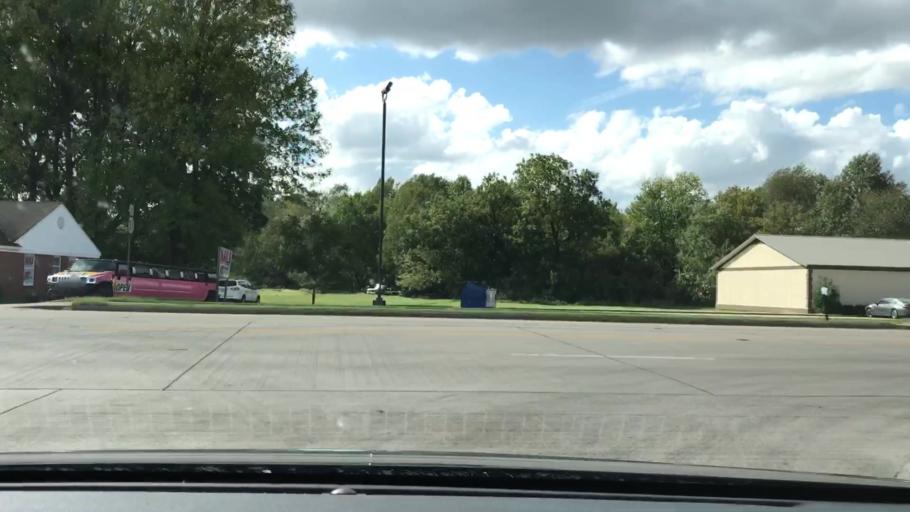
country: US
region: Kentucky
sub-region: Graves County
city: Mayfield
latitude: 36.7563
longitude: -88.6402
